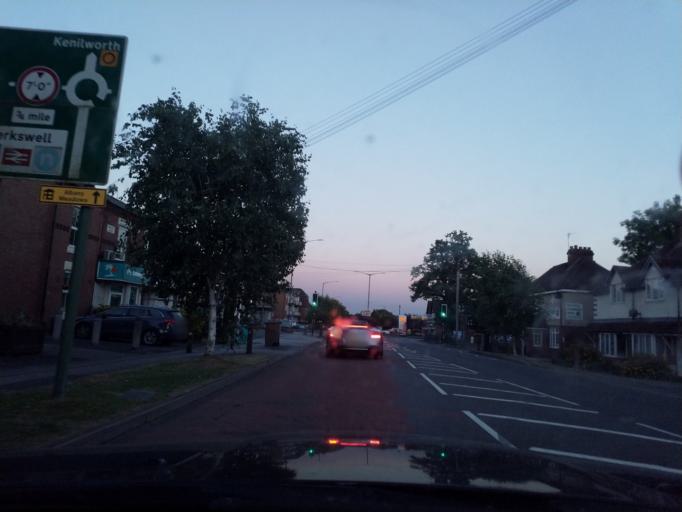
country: GB
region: England
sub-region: Solihull
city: Balsall Common
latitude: 52.3925
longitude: -1.6507
